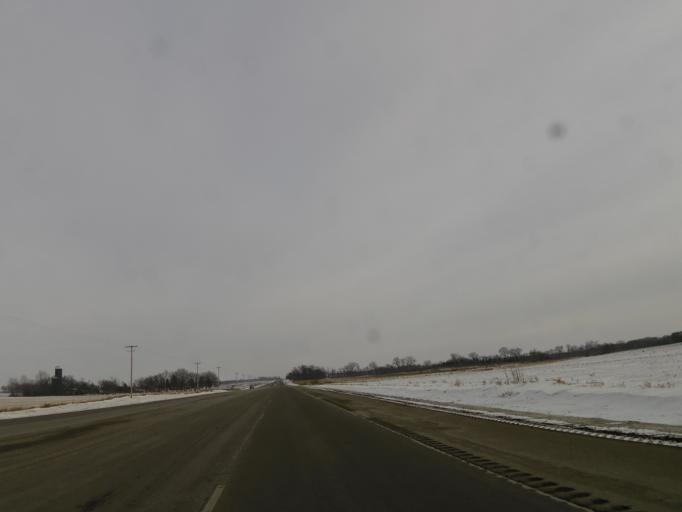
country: US
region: Minnesota
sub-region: McLeod County
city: Lester Prairie
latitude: 44.9067
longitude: -94.1299
